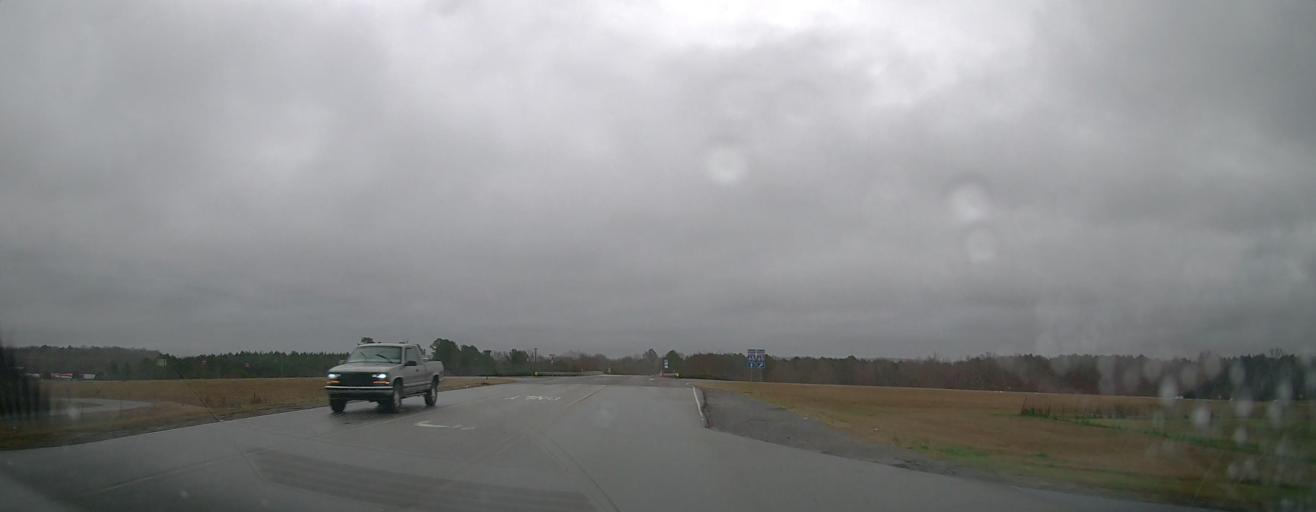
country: US
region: Alabama
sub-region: Morgan County
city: Falkville
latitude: 34.4125
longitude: -86.9005
